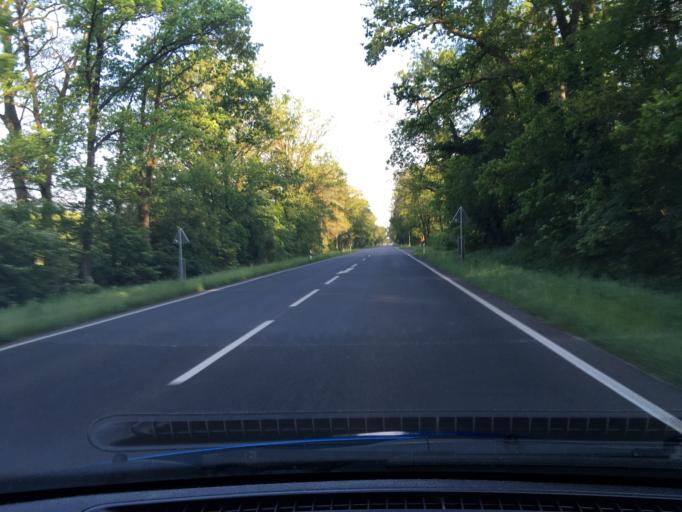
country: DE
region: Lower Saxony
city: Handeloh
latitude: 53.1982
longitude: 9.8274
